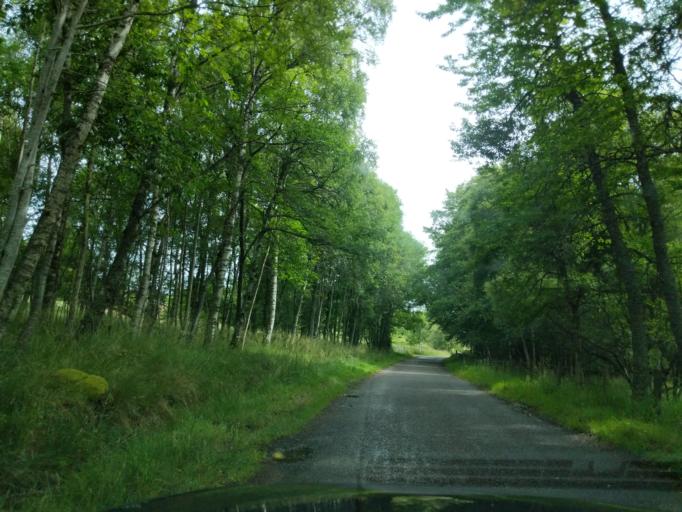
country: GB
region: Scotland
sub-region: Aberdeenshire
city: Aboyne
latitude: 57.0618
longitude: -2.8396
